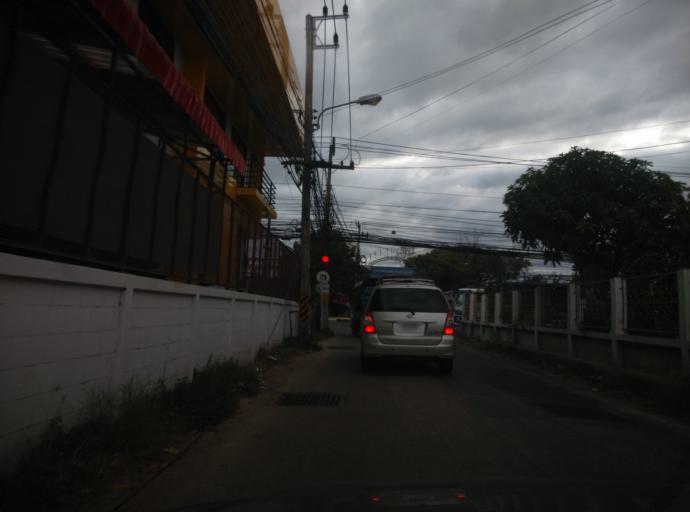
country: TH
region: Sisaket
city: Si Sa Ket
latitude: 15.1115
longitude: 104.3537
